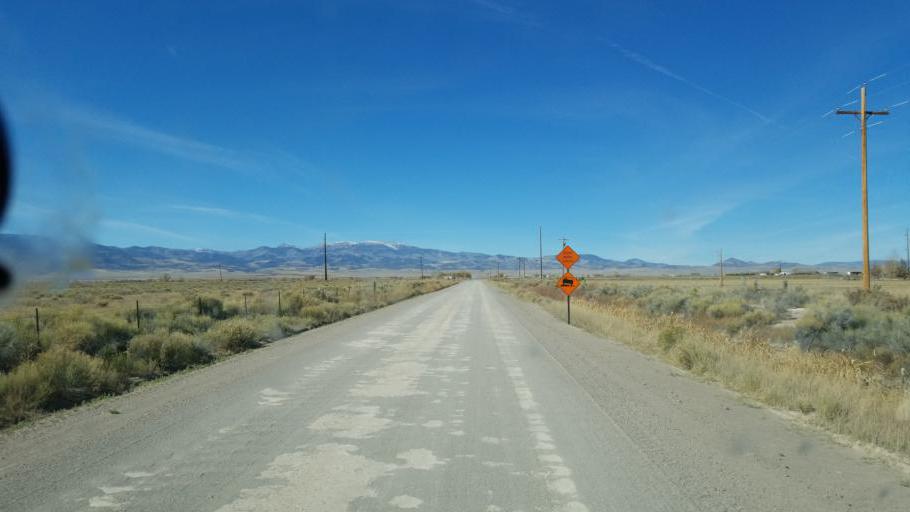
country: US
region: Colorado
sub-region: Rio Grande County
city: Monte Vista
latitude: 37.5313
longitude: -106.0909
